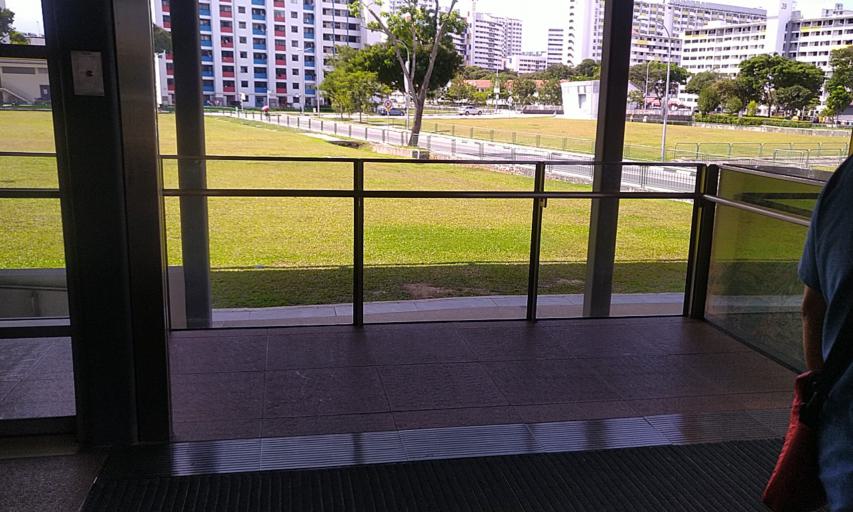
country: SG
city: Singapore
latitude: 1.3265
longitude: 103.8837
